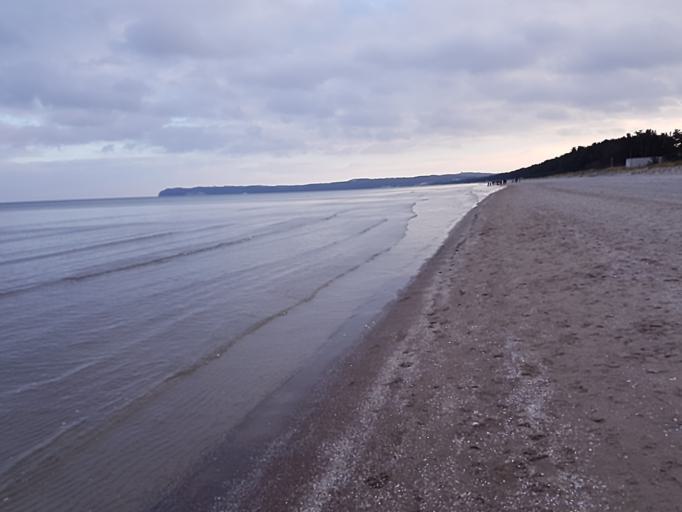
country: DE
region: Mecklenburg-Vorpommern
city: Ostseebad Binz
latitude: 54.4331
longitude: 13.5821
